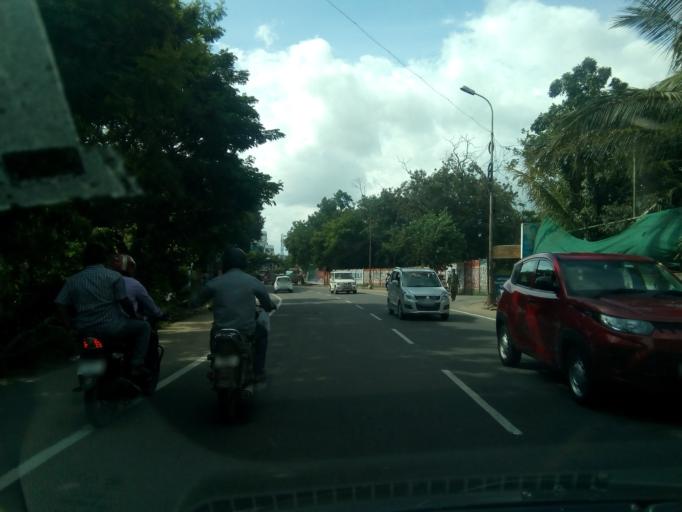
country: IN
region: Tamil Nadu
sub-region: Coimbatore
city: Singanallur
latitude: 11.0168
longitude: 77.0234
